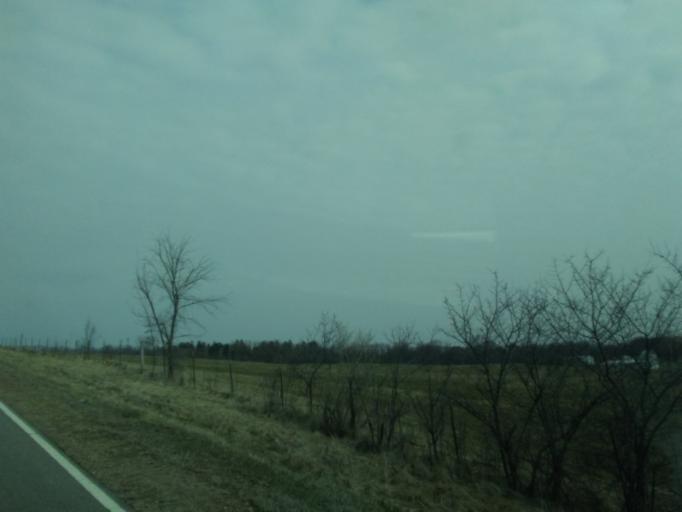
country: US
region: Wisconsin
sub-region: Columbia County
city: Lodi
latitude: 43.3056
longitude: -89.5415
